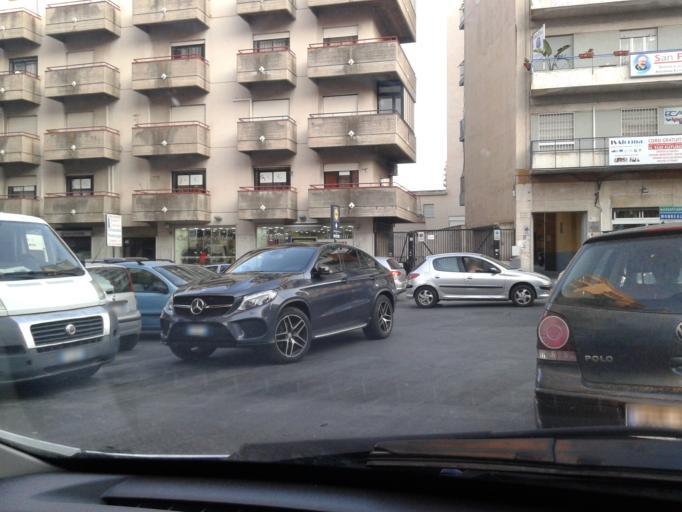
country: IT
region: Sicily
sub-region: Palermo
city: Palermo
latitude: 38.1047
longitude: 13.3338
